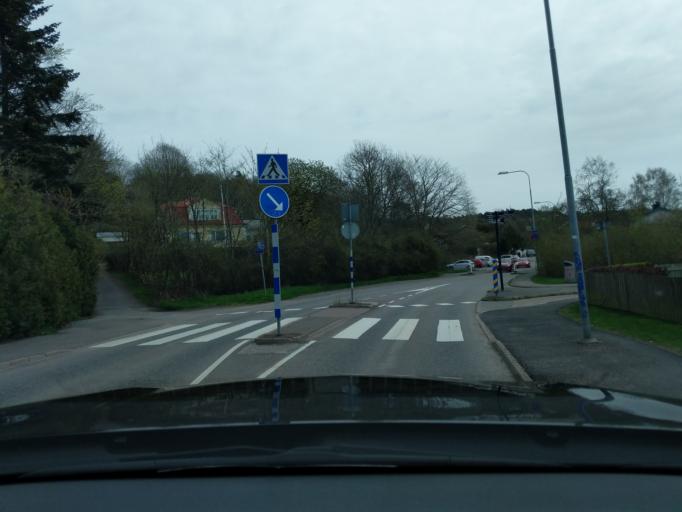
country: SE
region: Vaestra Goetaland
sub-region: Goteborg
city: Majorna
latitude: 57.6352
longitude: 11.9362
